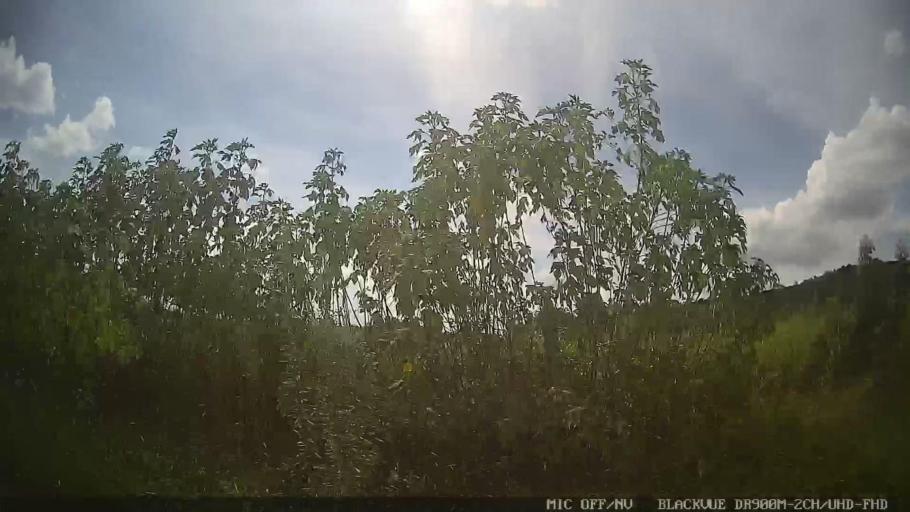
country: BR
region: Sao Paulo
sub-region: Atibaia
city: Atibaia
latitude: -23.0931
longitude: -46.5532
